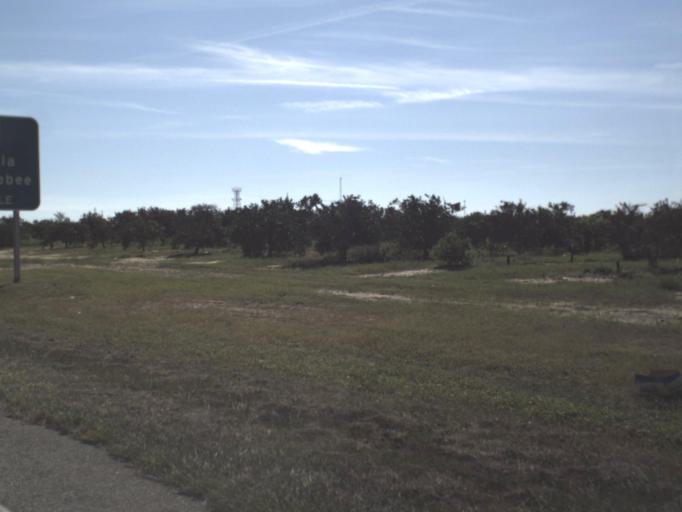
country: US
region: Florida
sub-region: Highlands County
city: Placid Lakes
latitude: 27.2166
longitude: -81.3288
